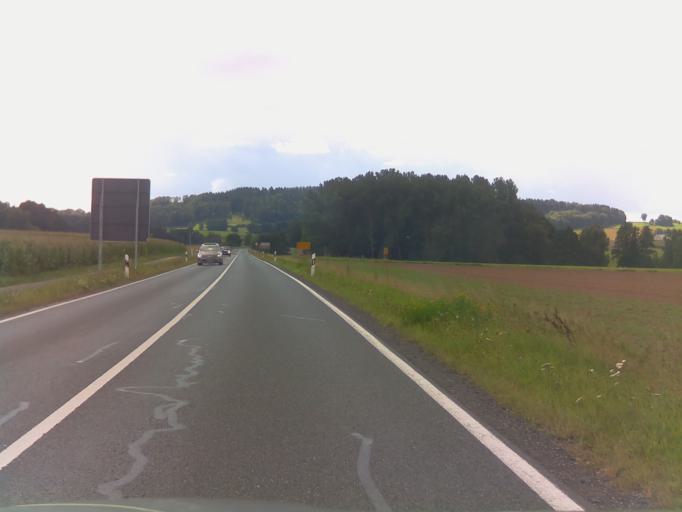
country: DE
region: Bavaria
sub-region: Upper Franconia
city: Neustadt bei Coburg
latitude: 50.3090
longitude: 11.1088
